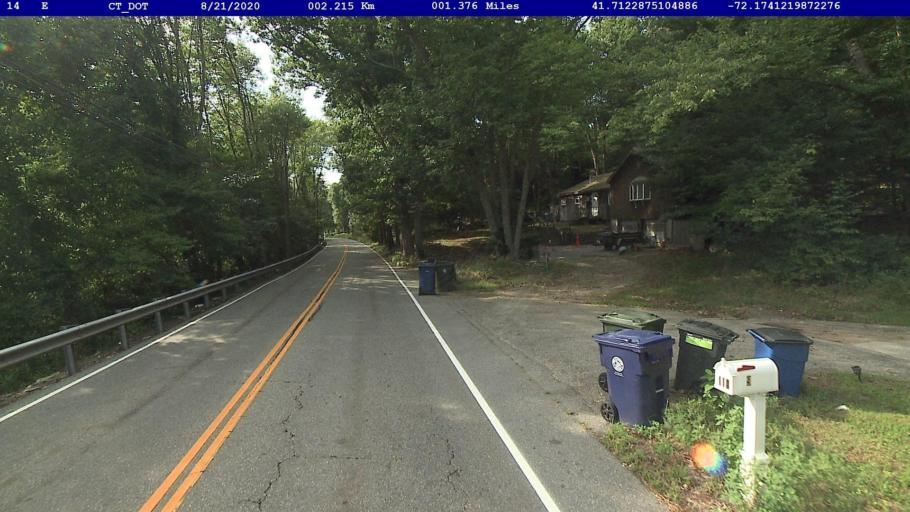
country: US
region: Connecticut
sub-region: Windham County
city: Windham
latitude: 41.7123
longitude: -72.1743
